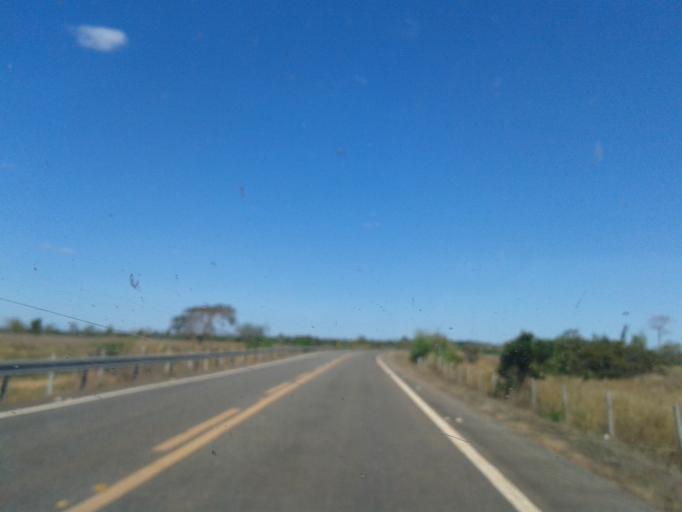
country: BR
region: Goias
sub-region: Sao Miguel Do Araguaia
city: Sao Miguel do Araguaia
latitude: -13.6273
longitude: -50.3127
